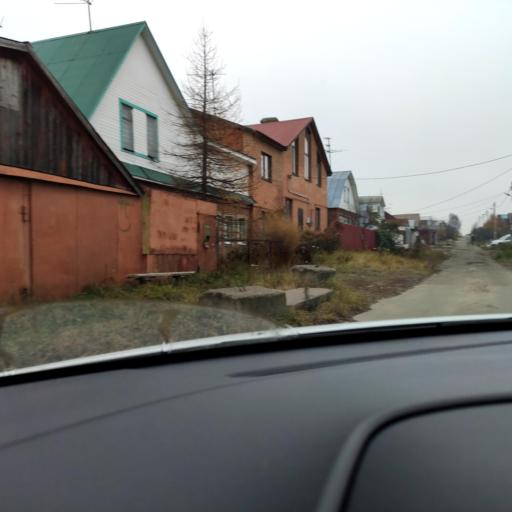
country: RU
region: Tatarstan
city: Vysokaya Gora
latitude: 55.8491
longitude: 49.2154
